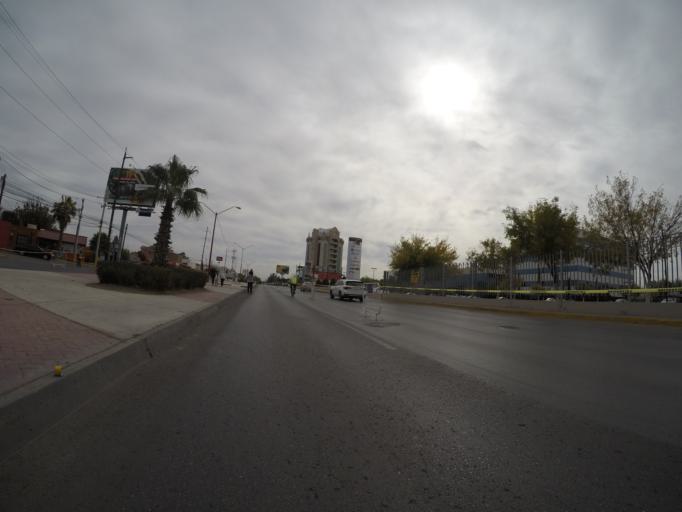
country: MX
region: Chihuahua
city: Ciudad Juarez
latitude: 31.7301
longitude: -106.4097
